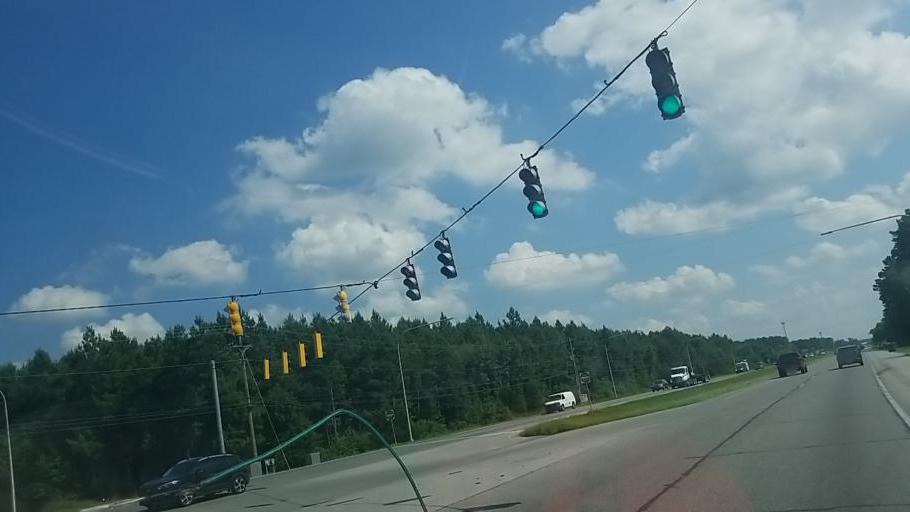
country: US
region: Delaware
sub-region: Sussex County
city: Georgetown
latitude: 38.7164
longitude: -75.4077
